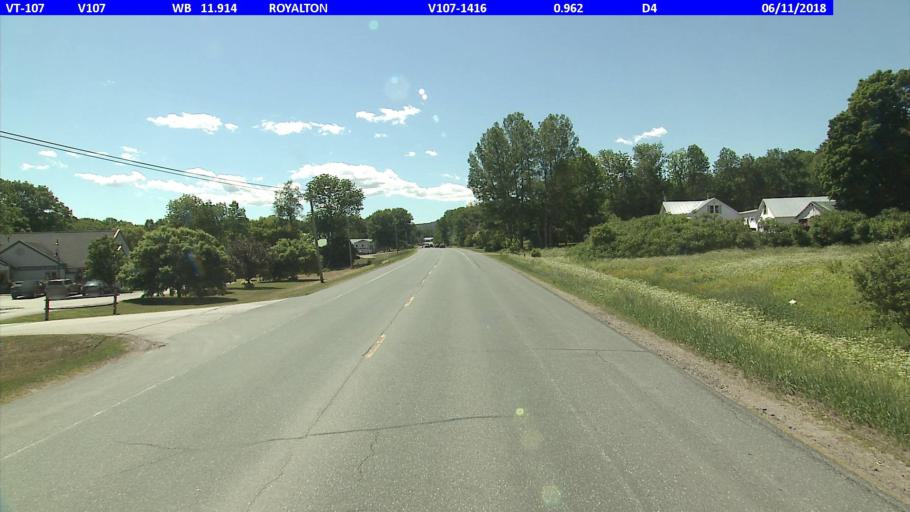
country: US
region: Vermont
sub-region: Orange County
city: Randolph
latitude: 43.8238
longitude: -72.5959
